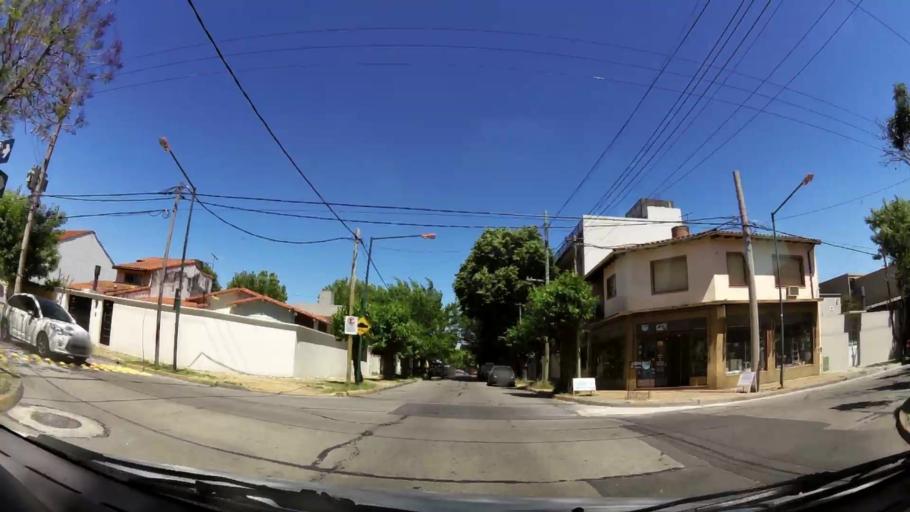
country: AR
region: Buenos Aires
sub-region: Partido de San Isidro
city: San Isidro
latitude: -34.4858
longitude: -58.5109
